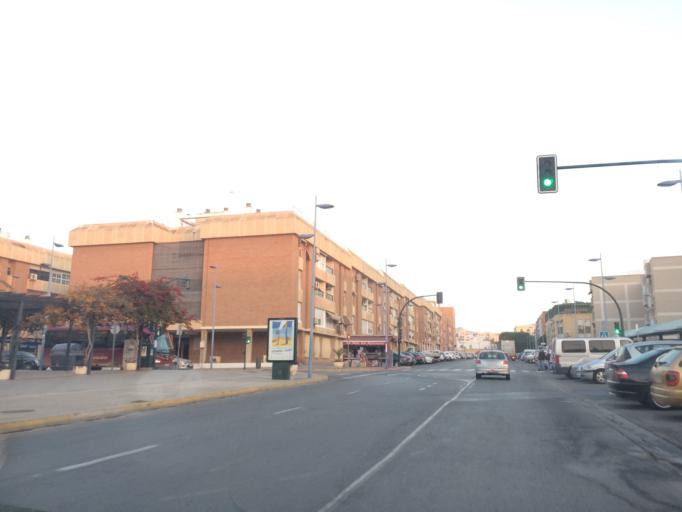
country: ES
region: Andalusia
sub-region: Provincia de Almeria
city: Almeria
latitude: 36.8410
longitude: -2.4497
